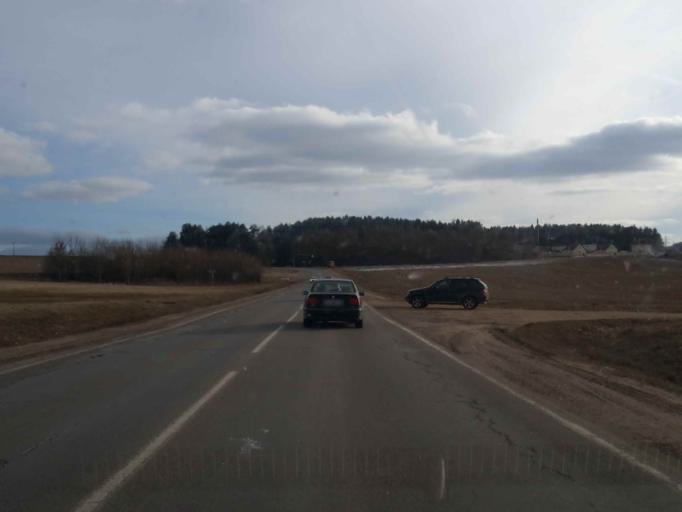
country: BY
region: Minsk
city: Bal'shavik
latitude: 54.0326
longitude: 27.5599
